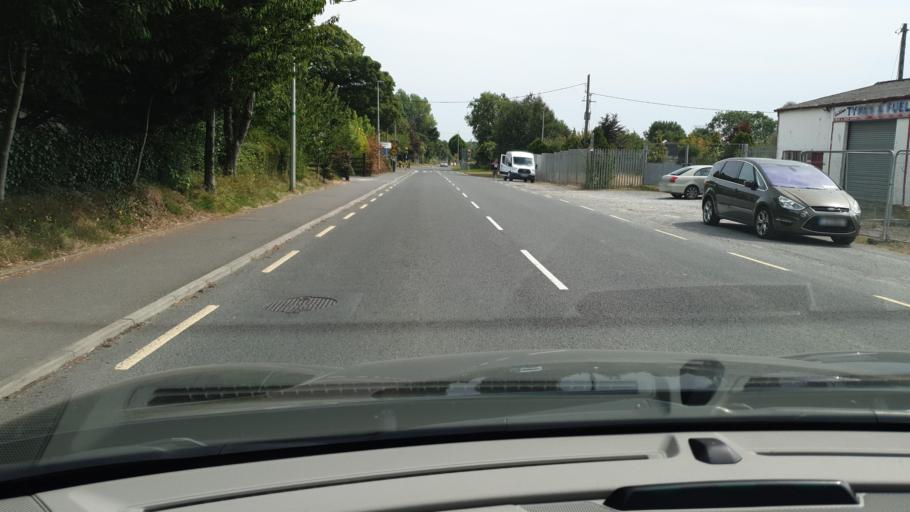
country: IE
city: Kentstown
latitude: 53.6278
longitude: -6.5350
